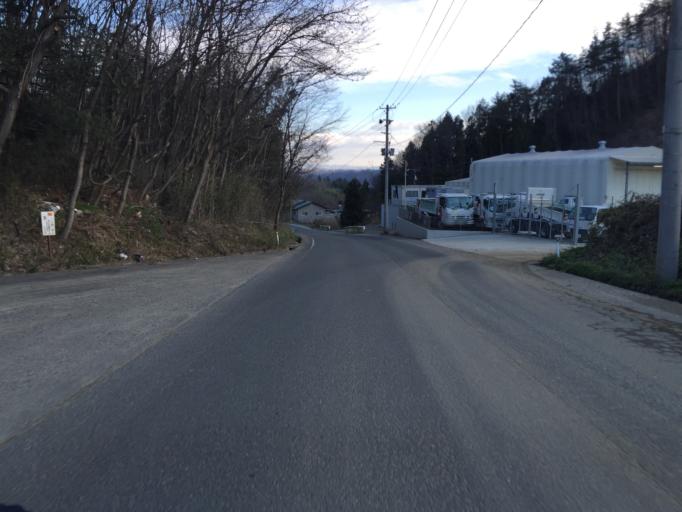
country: JP
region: Fukushima
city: Fukushima-shi
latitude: 37.7178
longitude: 140.4131
